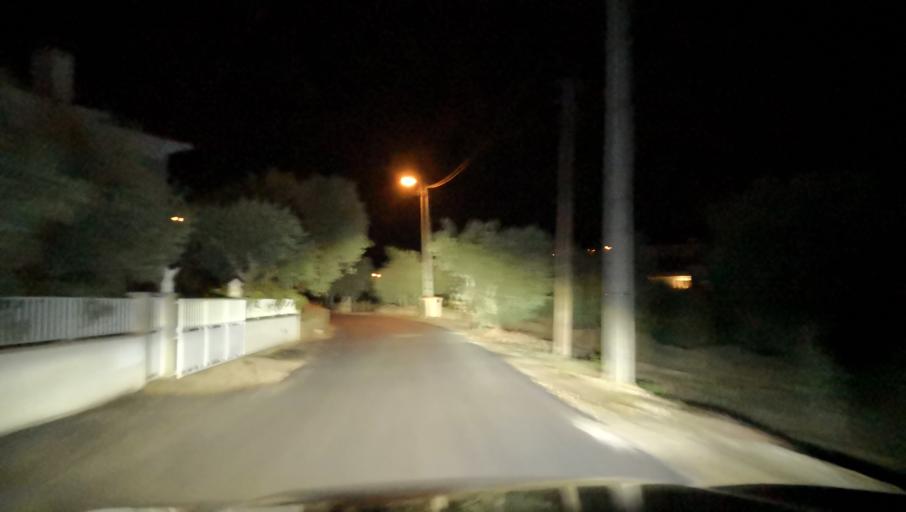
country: PT
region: Vila Real
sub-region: Sabrosa
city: Vilela
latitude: 41.2105
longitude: -7.6921
